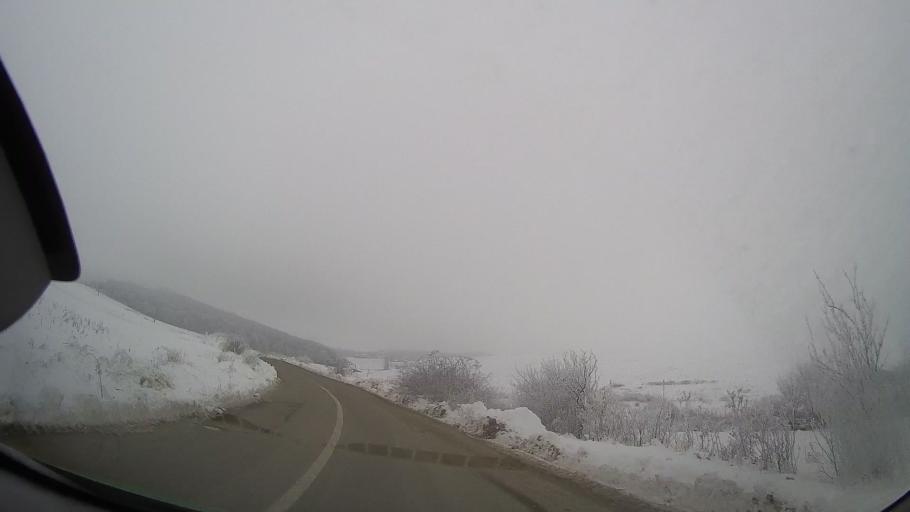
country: RO
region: Neamt
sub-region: Comuna Pancesti
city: Pancesti
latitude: 46.9186
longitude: 27.1632
